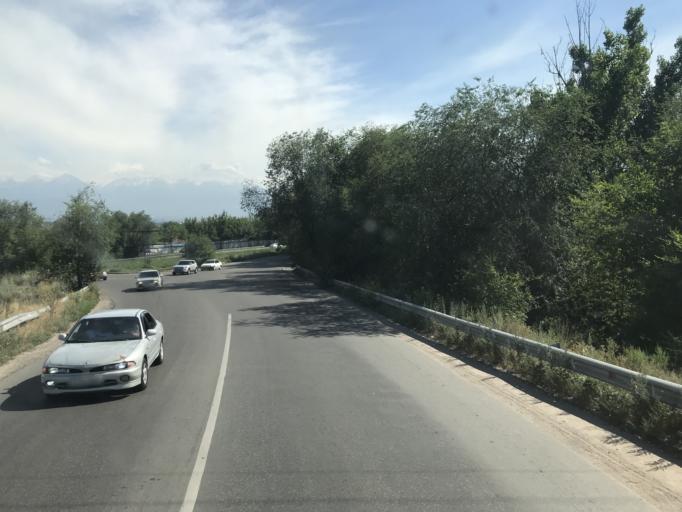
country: KZ
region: Almaty Oblysy
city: Pervomayskiy
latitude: 43.3515
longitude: 76.9056
